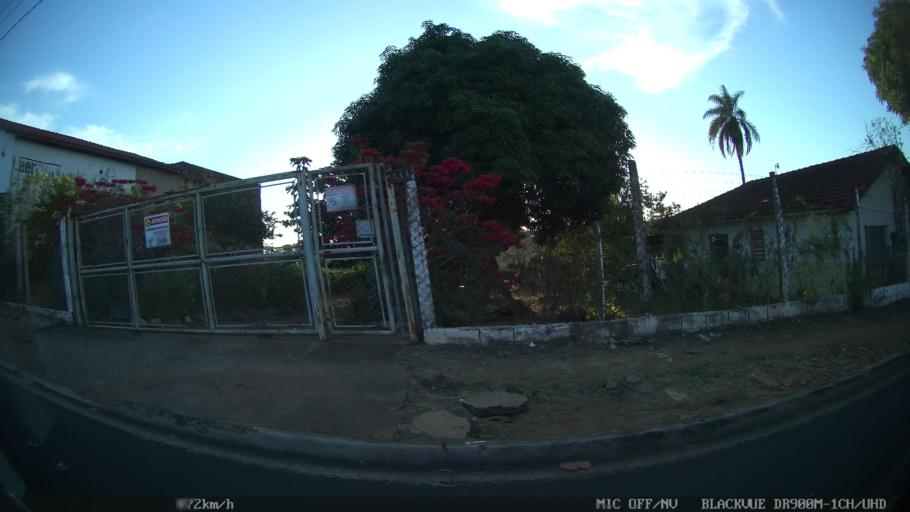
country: BR
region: Sao Paulo
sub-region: Franca
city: Franca
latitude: -20.5123
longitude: -47.4142
